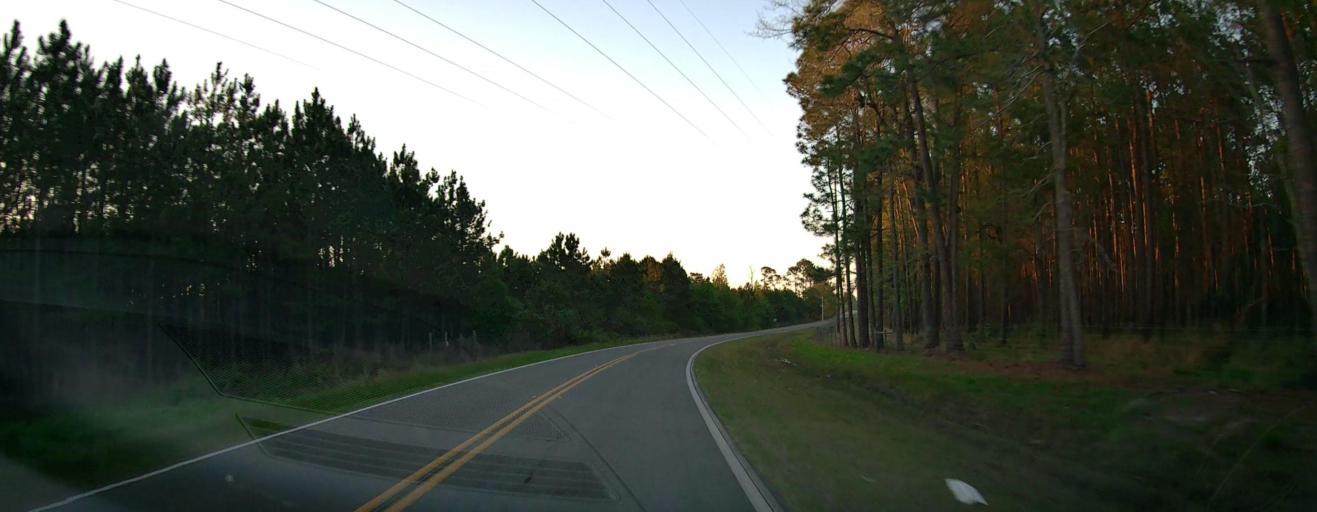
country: US
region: Georgia
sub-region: Ben Hill County
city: Fitzgerald
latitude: 31.7590
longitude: -83.3549
